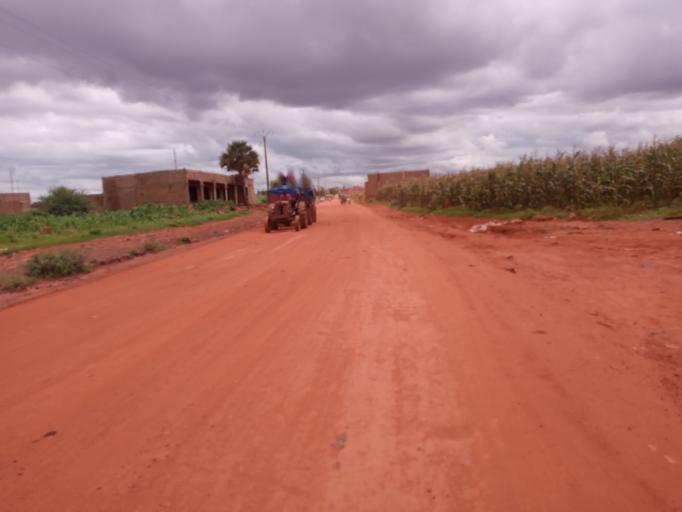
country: ML
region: Bamako
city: Bamako
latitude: 12.5450
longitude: -7.9942
